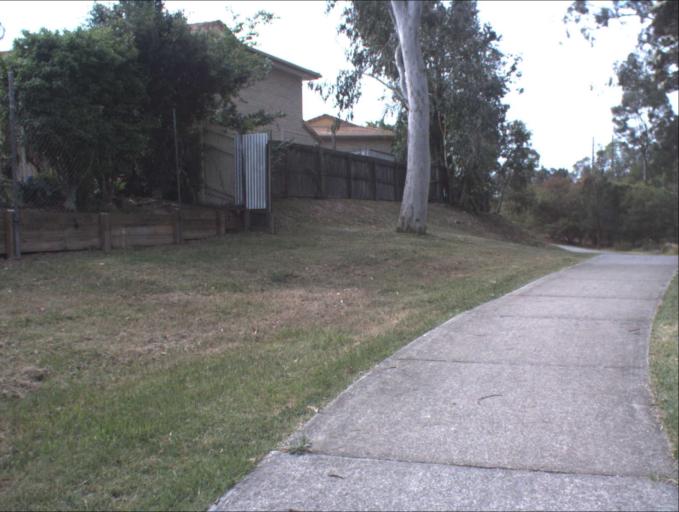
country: AU
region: Queensland
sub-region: Logan
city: Logan City
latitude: -27.6311
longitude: 153.1252
